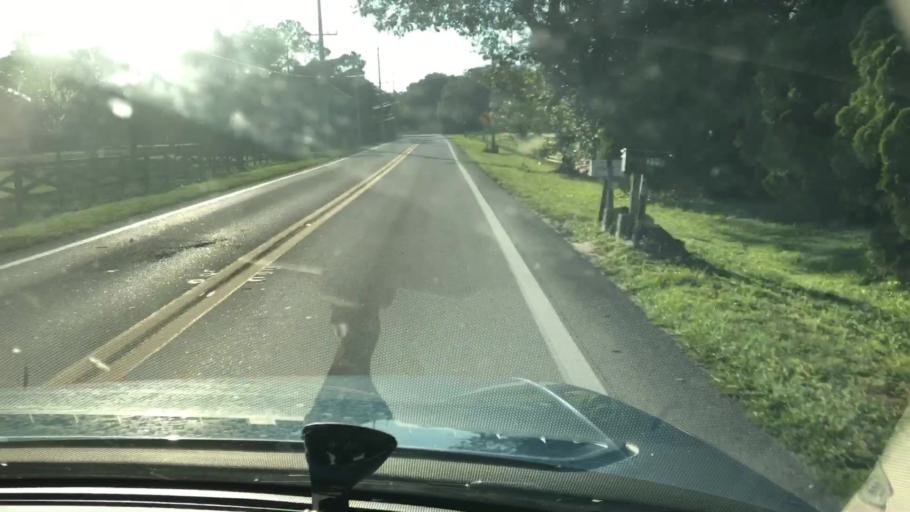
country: US
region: Florida
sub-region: Polk County
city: Gibsonia
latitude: 28.1575
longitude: -81.9114
